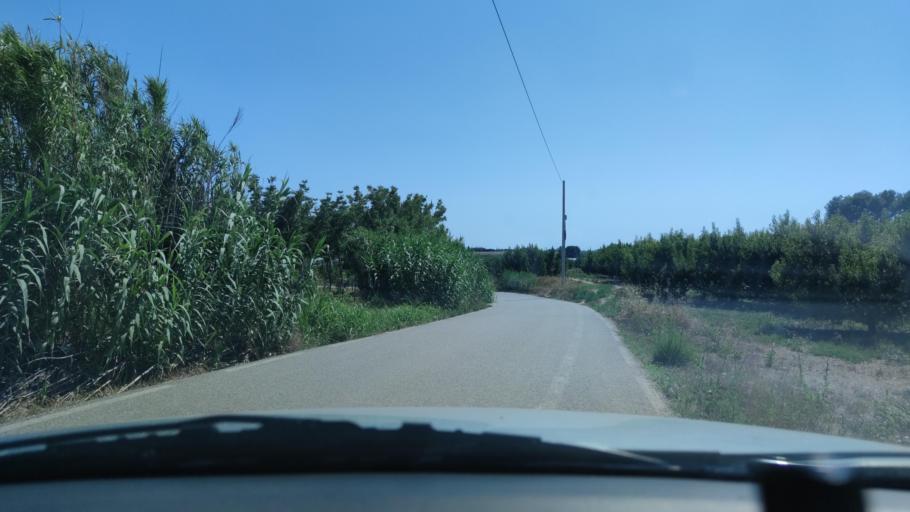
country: ES
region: Catalonia
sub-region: Provincia de Lleida
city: Torrefarrera
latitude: 41.6872
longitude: 0.6248
